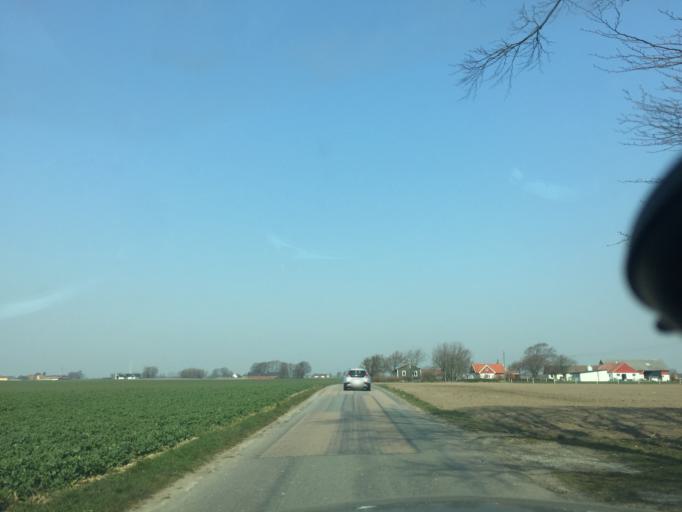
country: SE
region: Skane
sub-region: Simrishamns Kommun
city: Simrishamn
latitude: 55.4471
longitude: 14.2176
